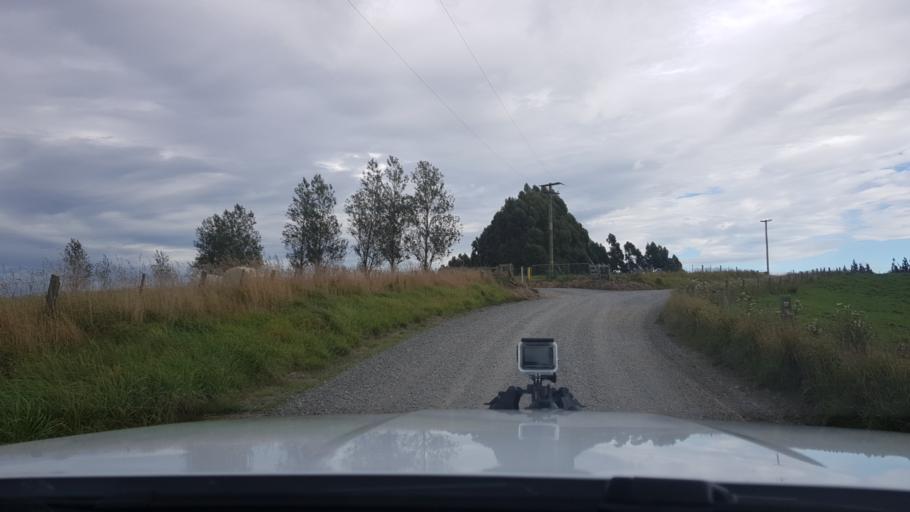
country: NZ
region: Otago
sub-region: Clutha District
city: Balclutha
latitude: -46.2132
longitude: 169.7376
